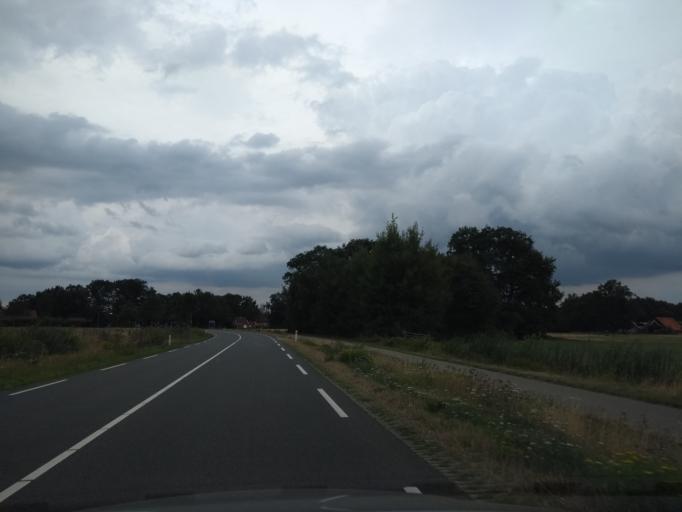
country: DE
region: Lower Saxony
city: Lage
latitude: 52.4008
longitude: 6.9554
